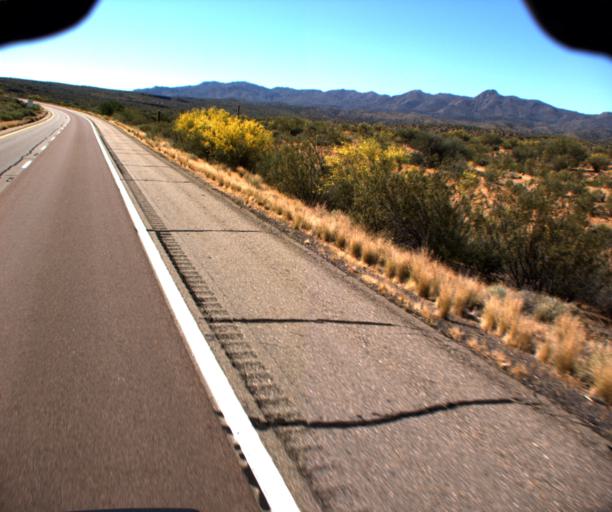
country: US
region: Arizona
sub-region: Yavapai County
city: Bagdad
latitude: 34.5106
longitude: -113.4160
